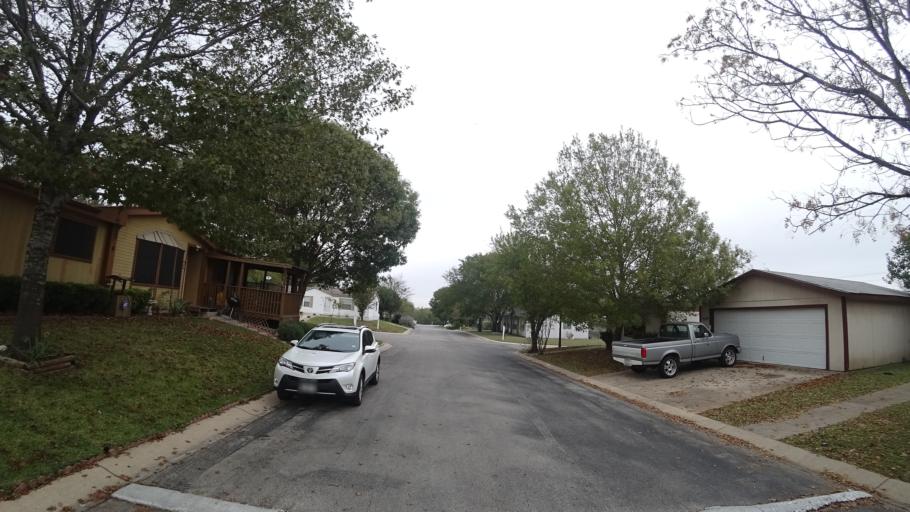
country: US
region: Texas
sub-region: Travis County
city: Pflugerville
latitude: 30.3913
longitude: -97.6403
